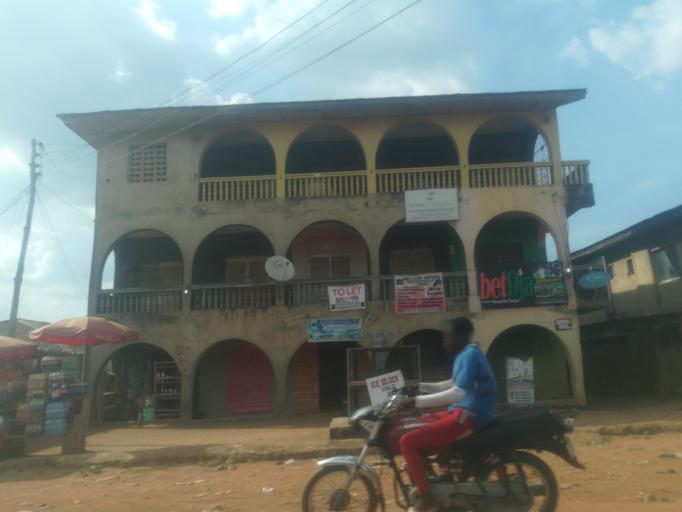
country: NG
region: Ogun
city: Abeokuta
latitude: 7.1167
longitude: 3.3167
